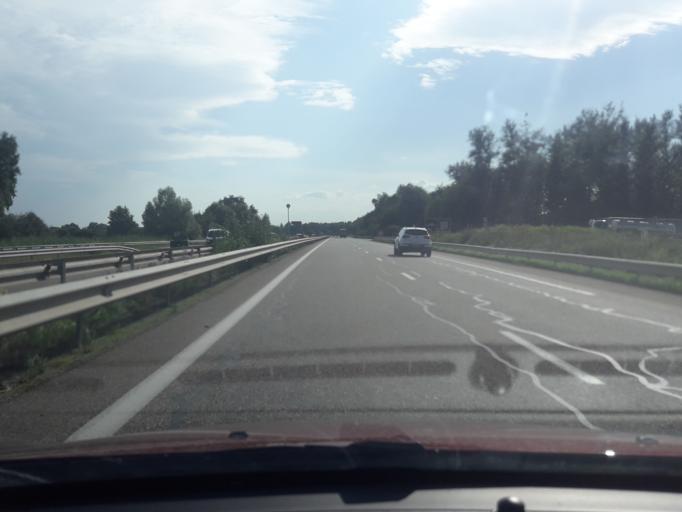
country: FR
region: Alsace
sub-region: Departement du Bas-Rhin
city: Kilstett
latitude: 48.6940
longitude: 7.8308
